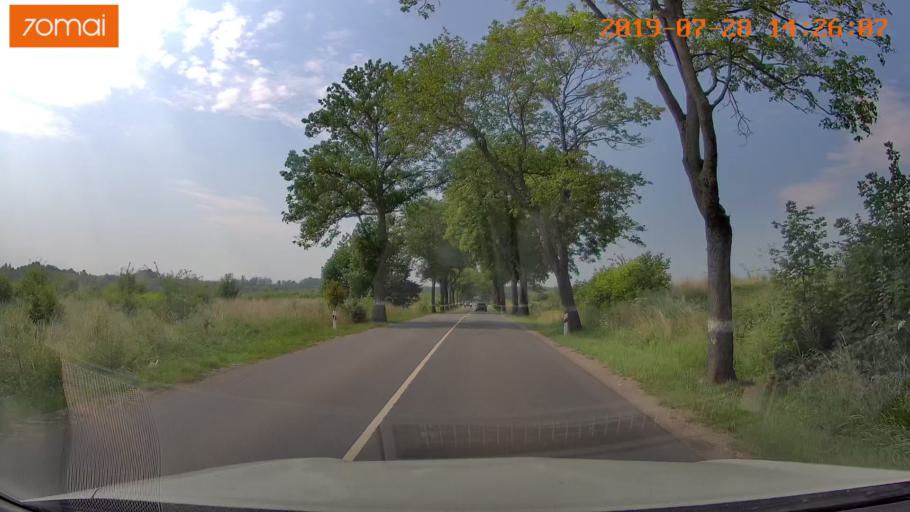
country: RU
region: Kaliningrad
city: Otradnoye
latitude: 54.8130
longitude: 20.1219
